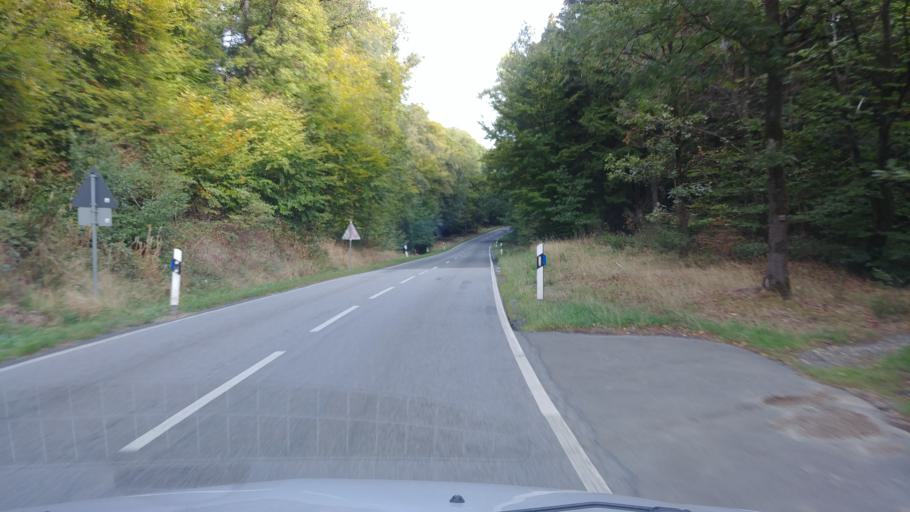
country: DE
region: Rheinland-Pfalz
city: Reckenroth
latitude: 50.1763
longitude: 8.0104
